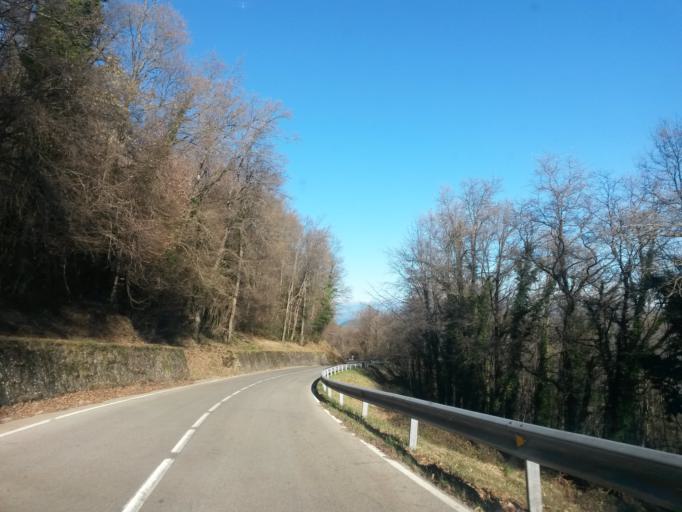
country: ES
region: Catalonia
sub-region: Provincia de Girona
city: Sant Feliu de Pallerols
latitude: 42.0549
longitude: 2.5061
